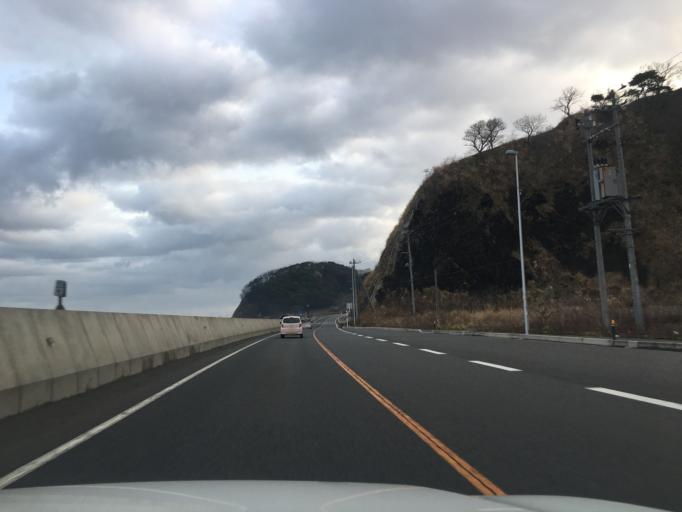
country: JP
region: Yamagata
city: Tsuruoka
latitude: 38.5873
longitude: 139.5612
